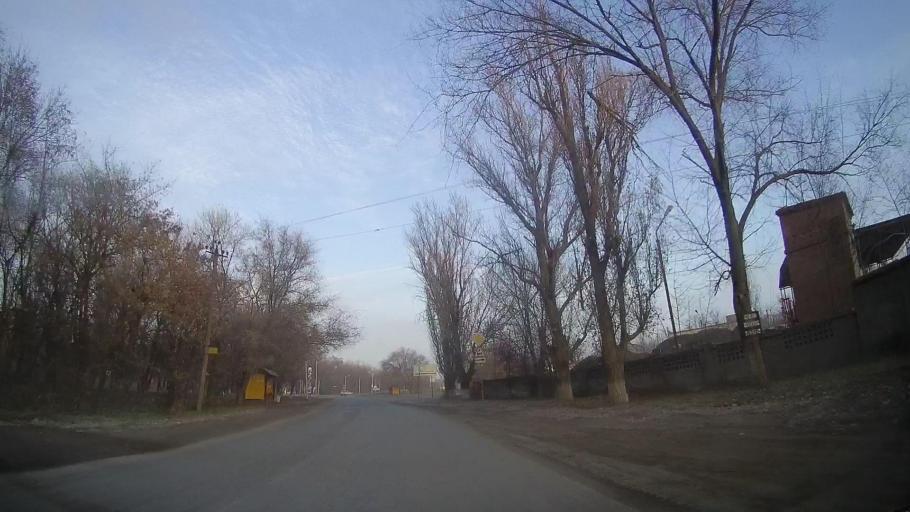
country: RU
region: Rostov
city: Bataysk
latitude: 47.1011
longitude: 39.7614
